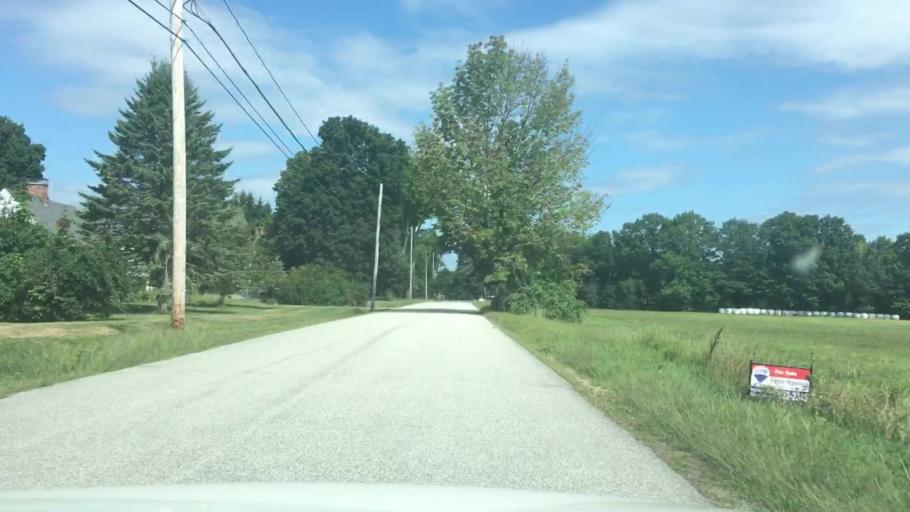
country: US
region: Maine
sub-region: Androscoggin County
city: Auburn
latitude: 44.1742
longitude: -70.2520
